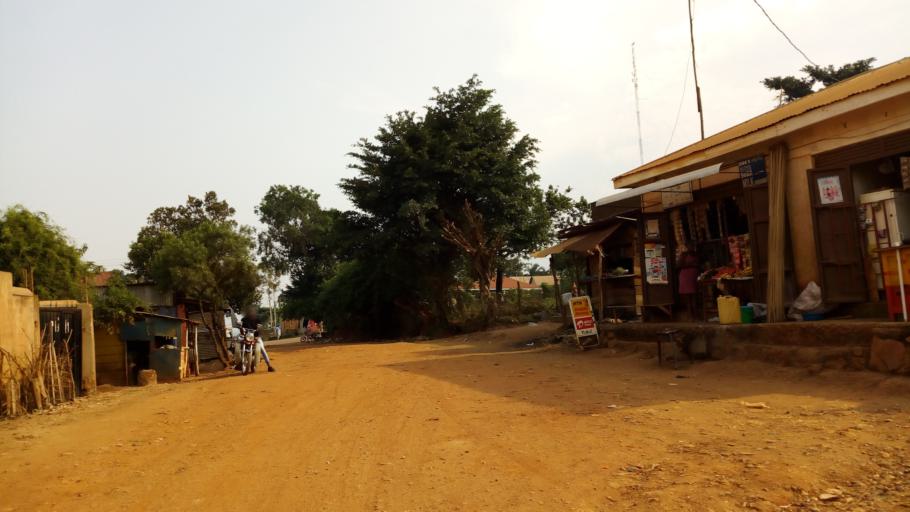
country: UG
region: Central Region
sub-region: Wakiso District
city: Kireka
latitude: 0.3104
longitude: 32.6498
